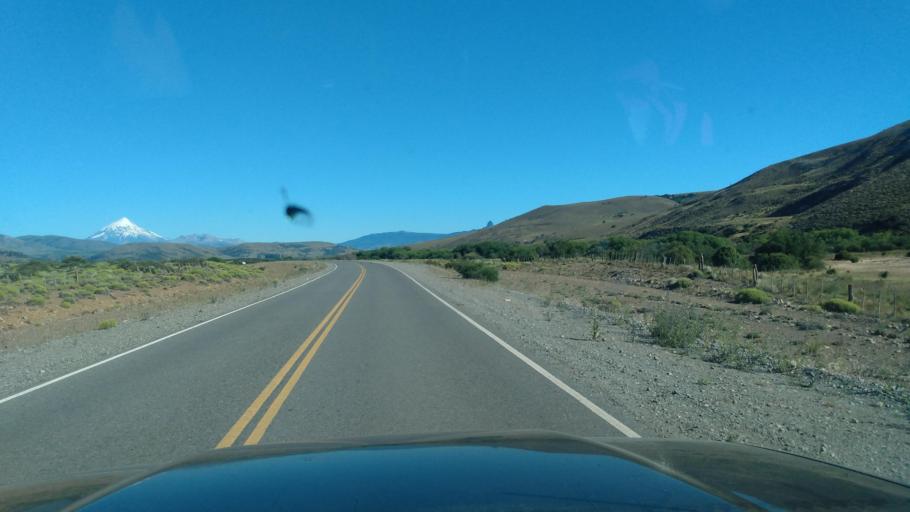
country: AR
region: Neuquen
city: Junin de los Andes
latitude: -39.8924
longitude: -71.1505
